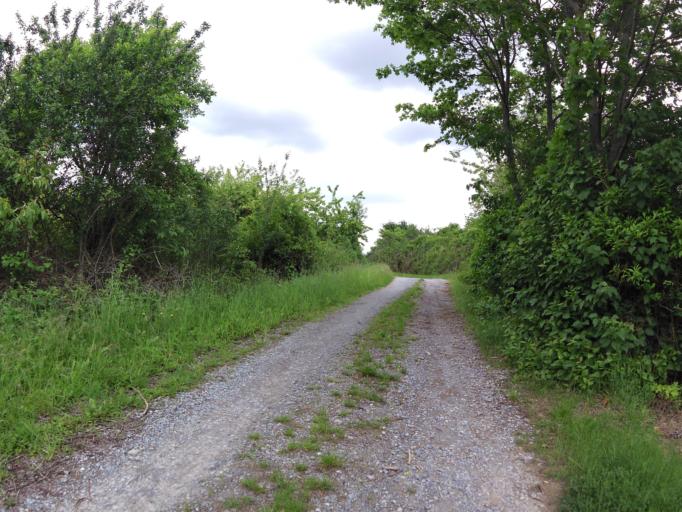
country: DE
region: Bavaria
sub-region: Regierungsbezirk Unterfranken
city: Sommerhausen
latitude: 49.7239
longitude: 10.0284
